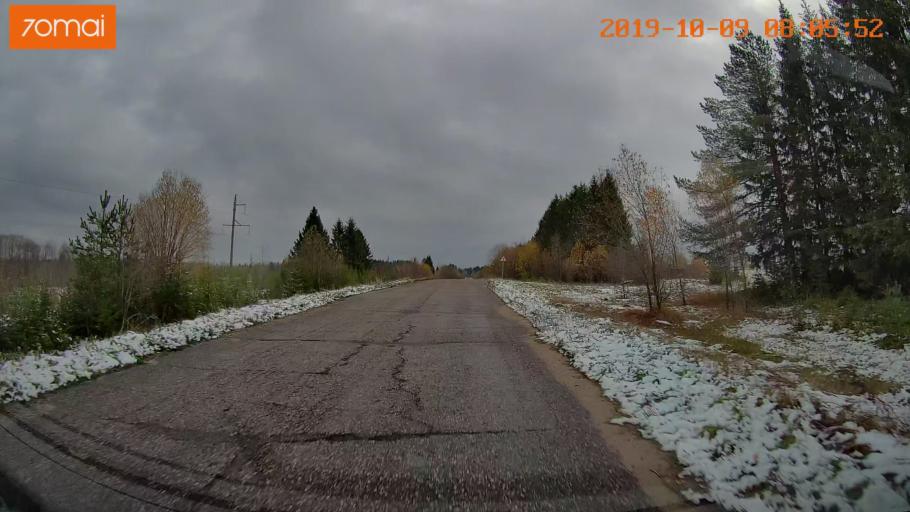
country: RU
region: Jaroslavl
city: Kukoboy
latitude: 58.6922
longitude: 40.0521
